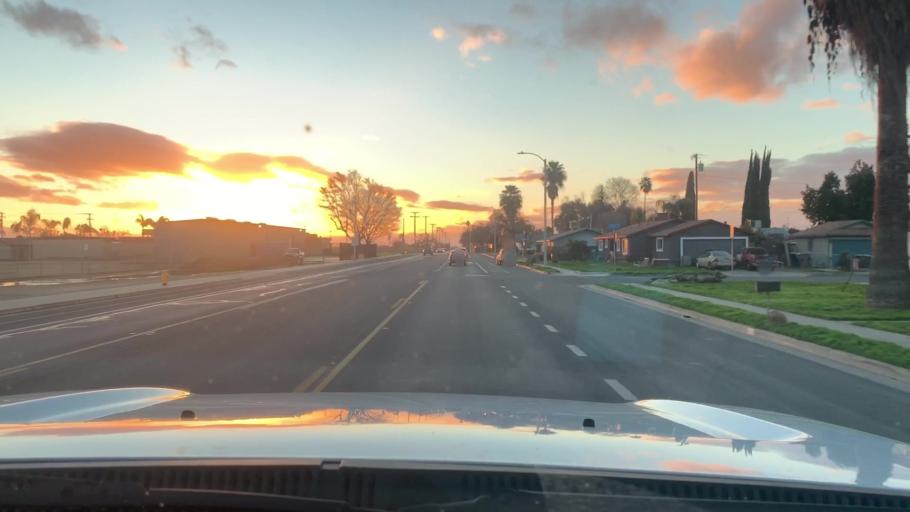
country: US
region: California
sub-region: Tulare County
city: Tulare
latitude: 36.1965
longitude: -119.3554
